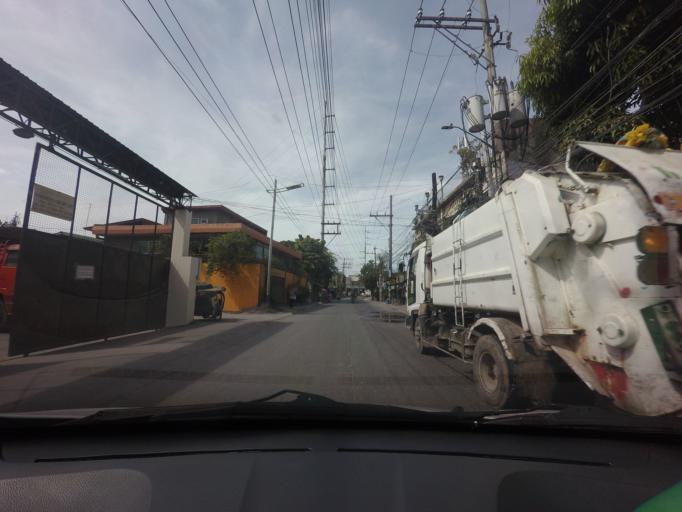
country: PH
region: Calabarzon
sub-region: Province of Rizal
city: Pateros
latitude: 14.5418
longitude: 121.0886
